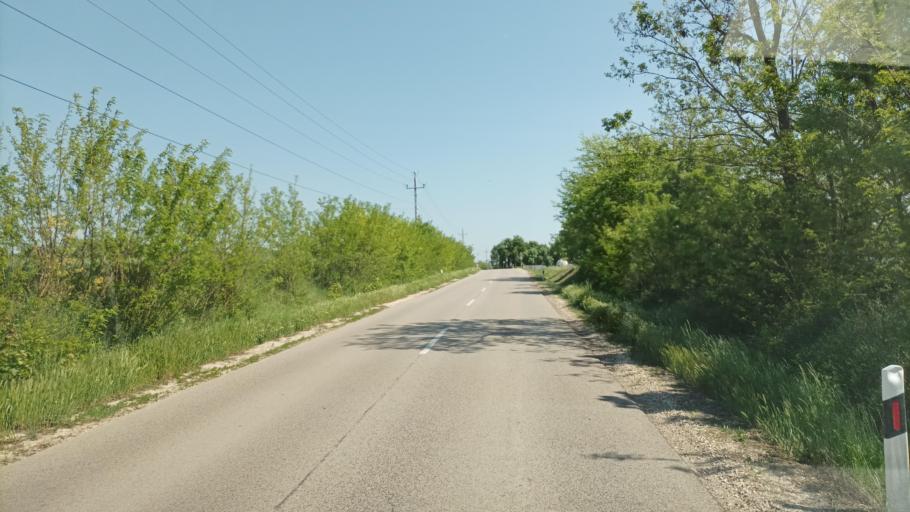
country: HU
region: Pest
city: Suelysap
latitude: 47.4336
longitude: 19.5324
